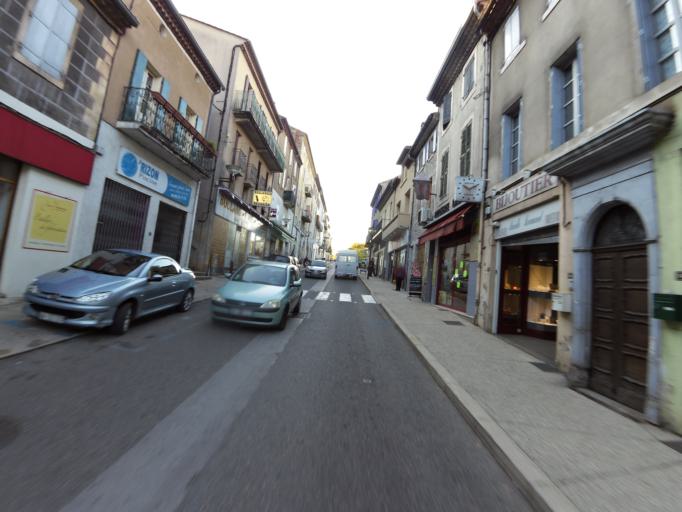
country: FR
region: Rhone-Alpes
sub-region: Departement de l'Ardeche
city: Joyeuse
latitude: 44.4799
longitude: 4.2370
